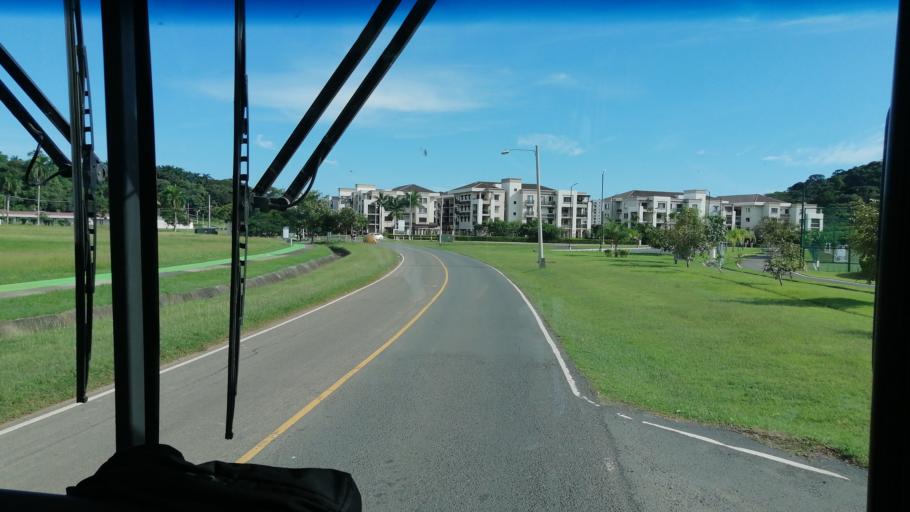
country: PA
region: Panama
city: Veracruz
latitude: 8.9082
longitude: -79.5919
